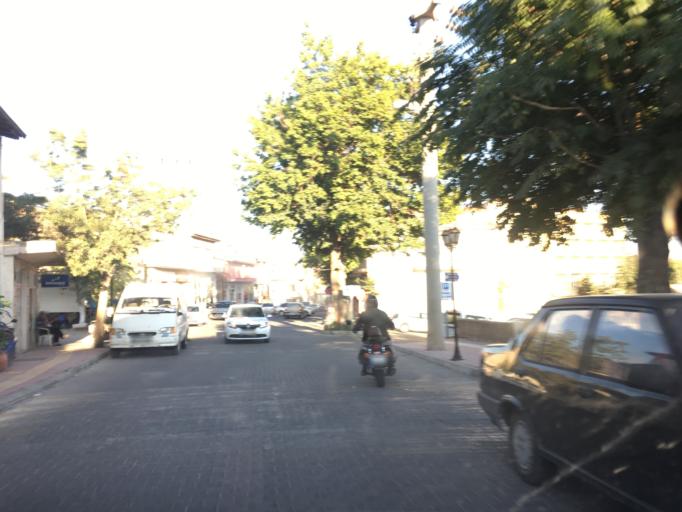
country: TR
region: Nevsehir
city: Avanos
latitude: 38.7178
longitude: 34.8420
